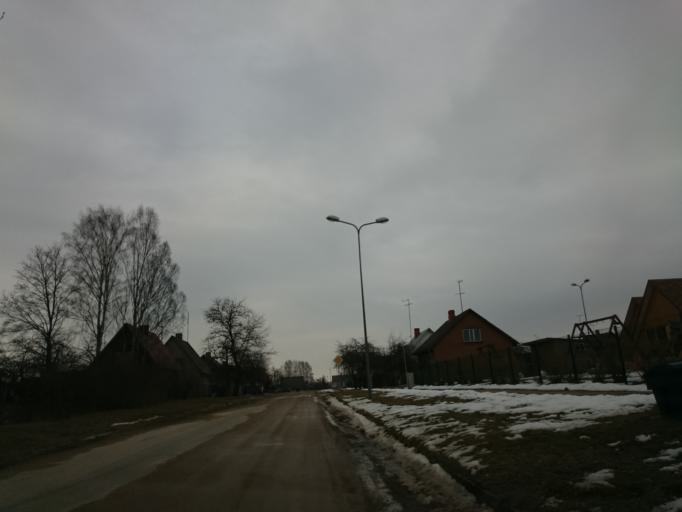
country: LV
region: Cesu Rajons
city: Cesis
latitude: 57.3197
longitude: 25.2695
